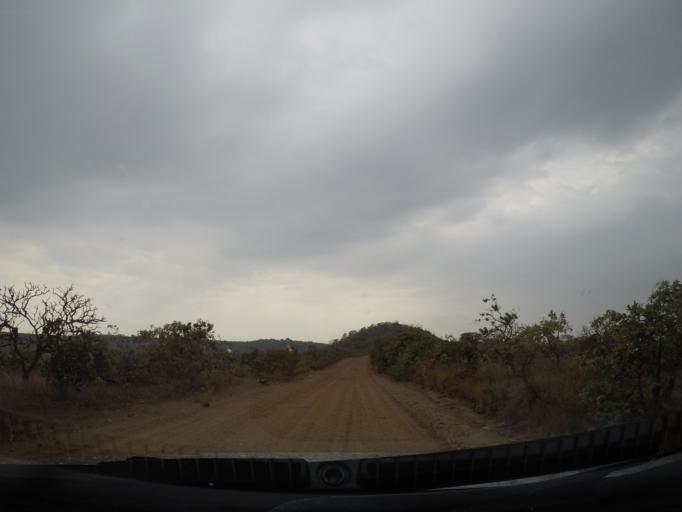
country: BR
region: Goias
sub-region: Pirenopolis
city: Pirenopolis
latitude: -15.8208
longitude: -48.9052
